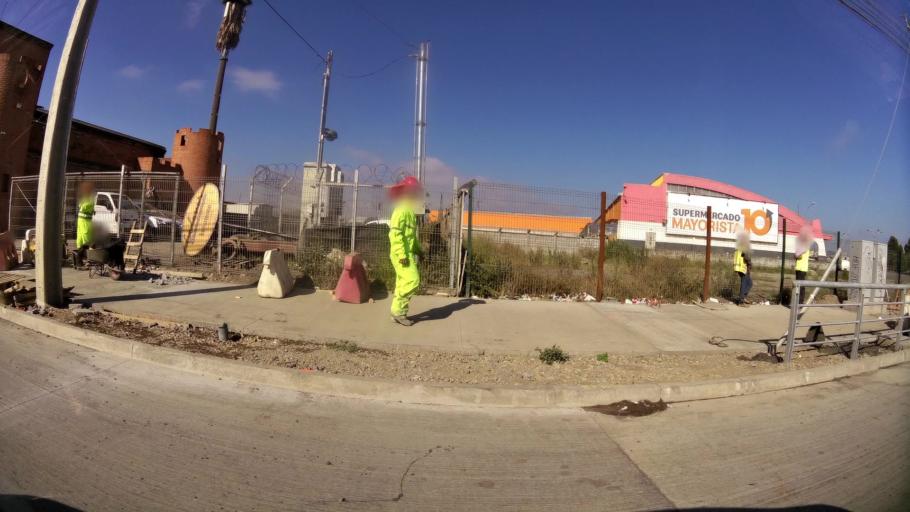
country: CL
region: Biobio
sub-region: Provincia de Concepcion
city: Concepcion
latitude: -36.7985
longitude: -73.0853
